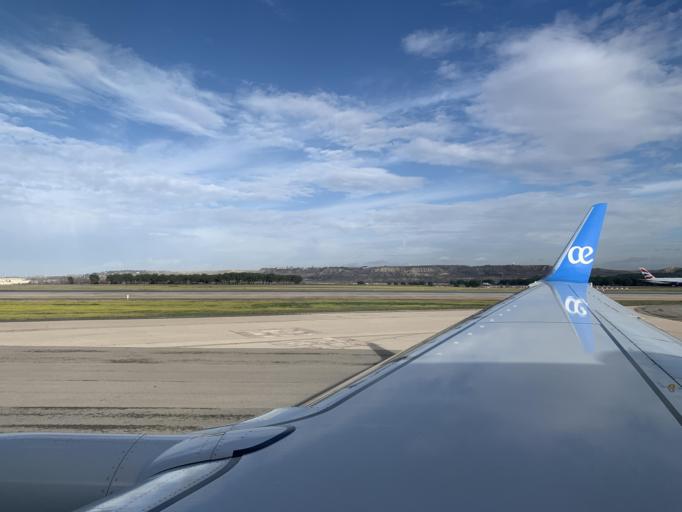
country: ES
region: Madrid
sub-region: Provincia de Madrid
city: Barajas de Madrid
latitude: 40.4781
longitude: -3.5718
